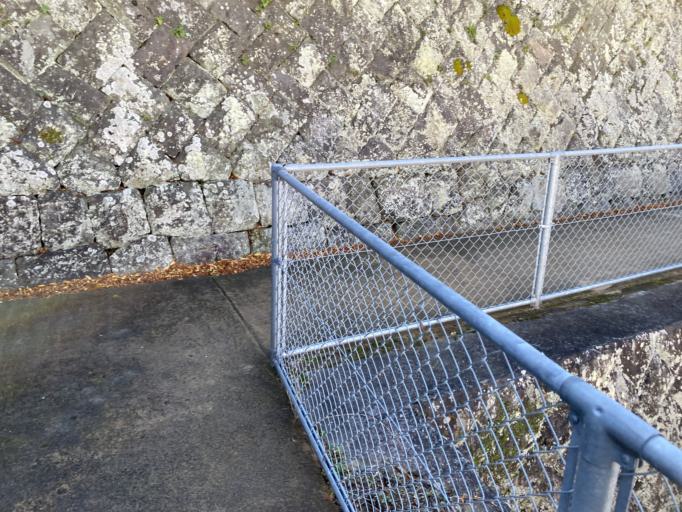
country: JP
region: Nagasaki
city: Nagasaki-shi
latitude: 32.7764
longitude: 129.8683
